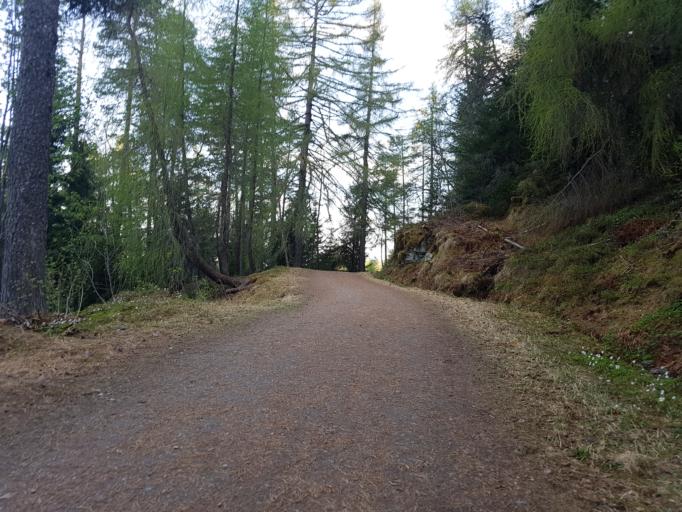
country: NO
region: Sor-Trondelag
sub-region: Trondheim
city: Trondheim
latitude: 63.4371
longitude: 10.3407
